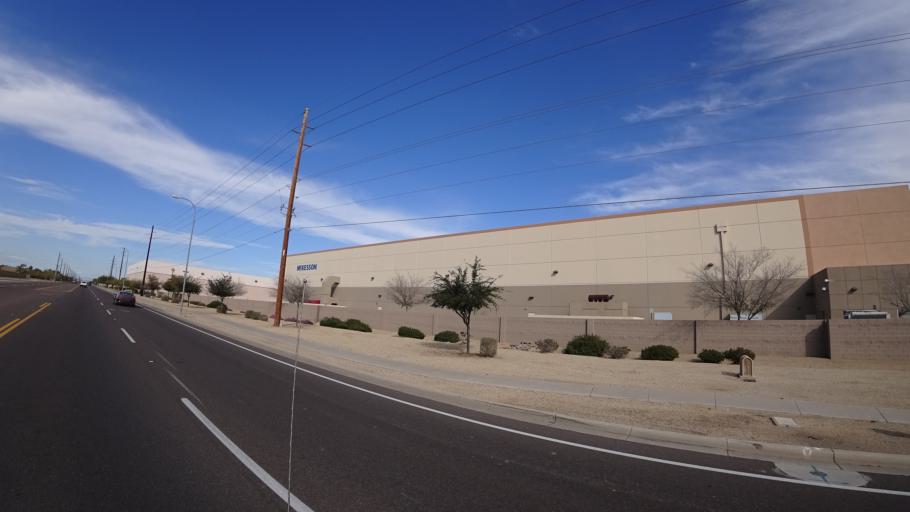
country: US
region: Arizona
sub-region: Maricopa County
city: Tolleson
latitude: 33.4400
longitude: -112.2898
